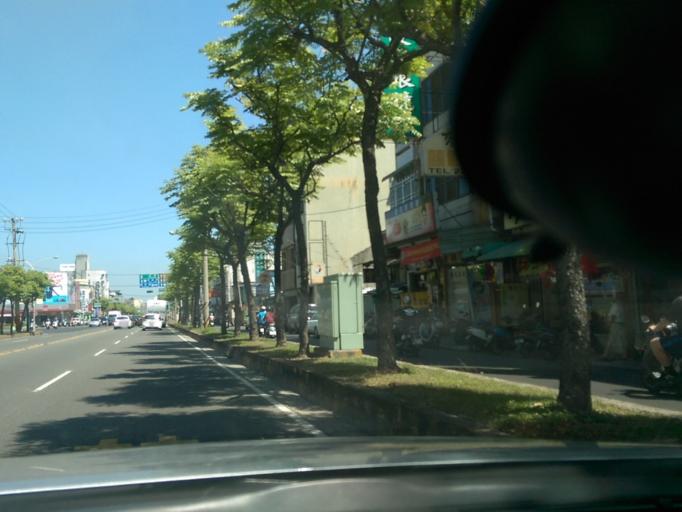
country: TW
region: Taiwan
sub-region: Chiayi
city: Jiayi Shi
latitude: 23.4681
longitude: 120.4545
